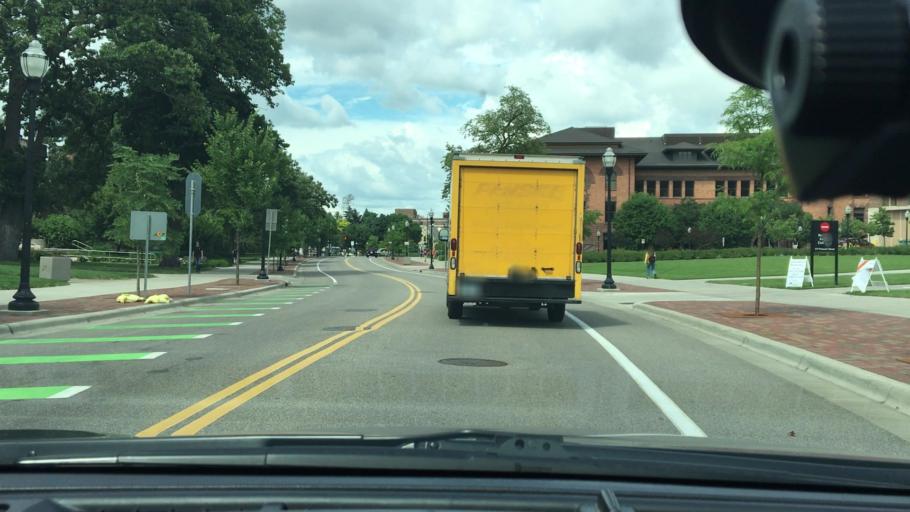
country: US
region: Minnesota
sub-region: Hennepin County
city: Minneapolis
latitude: 44.9762
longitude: -93.2367
